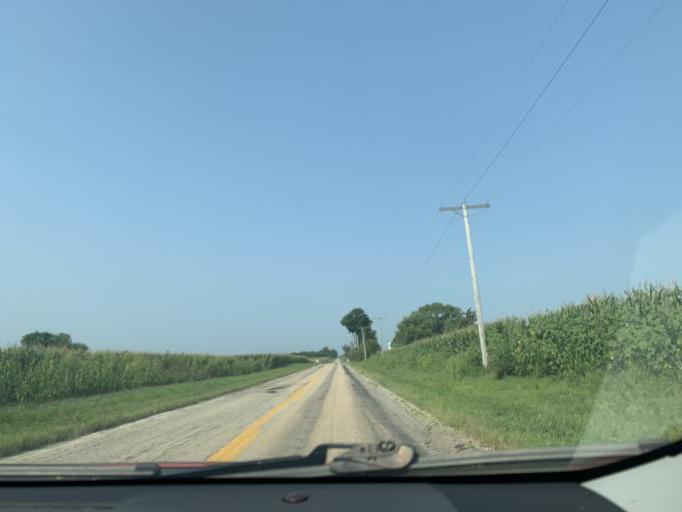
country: US
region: Illinois
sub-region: Whiteside County
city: Morrison
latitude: 41.8480
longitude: -89.8446
